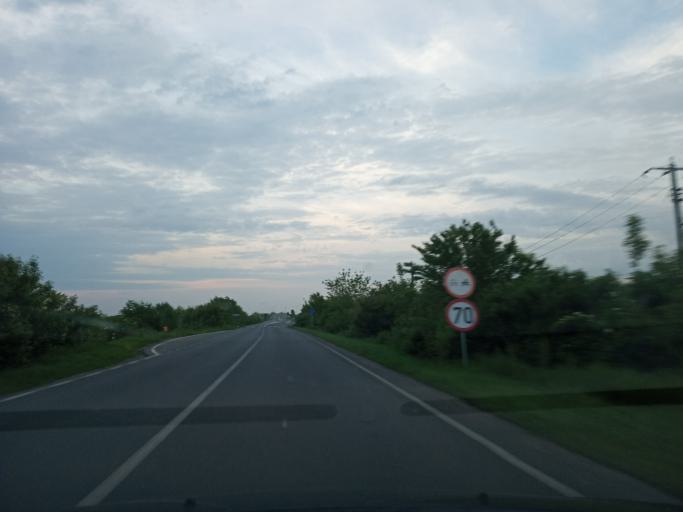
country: RO
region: Timis
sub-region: Comuna Voiteg
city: Voiteg
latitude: 45.4574
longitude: 21.2347
